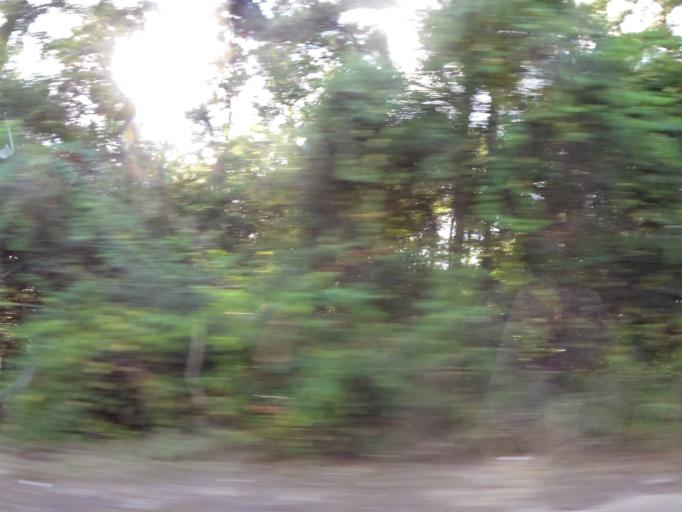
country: US
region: Georgia
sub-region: Brooks County
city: Quitman
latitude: 30.7780
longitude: -83.5605
